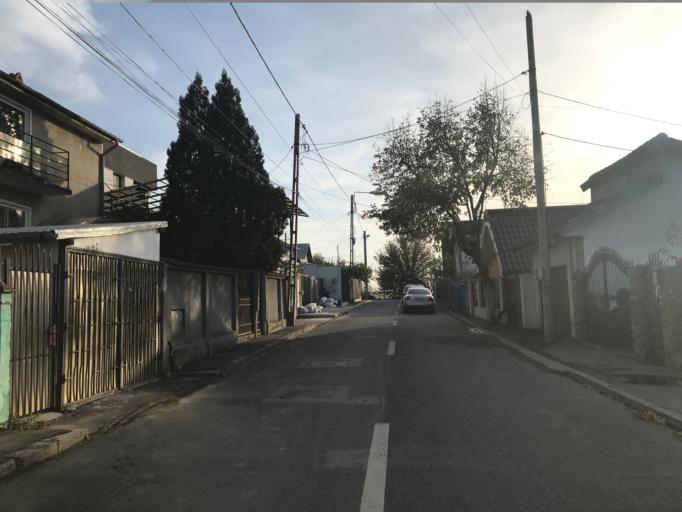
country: RO
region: Olt
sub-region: Municipiul Slatina
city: Slatina
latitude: 44.4244
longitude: 24.3552
